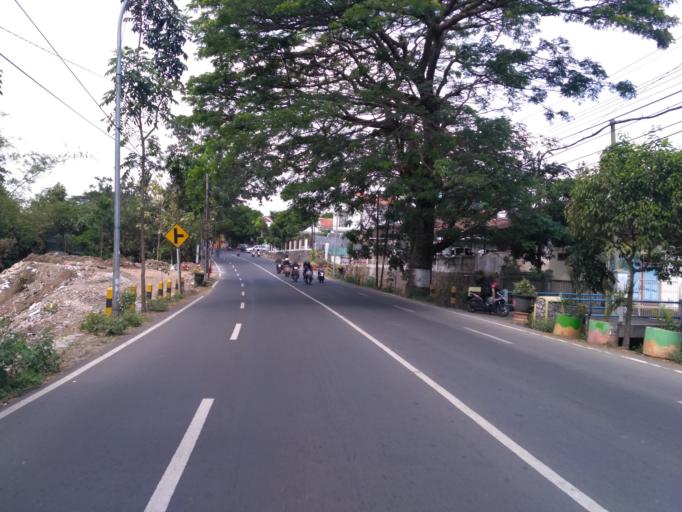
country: ID
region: East Java
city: Batu
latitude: -7.9080
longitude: 112.5787
